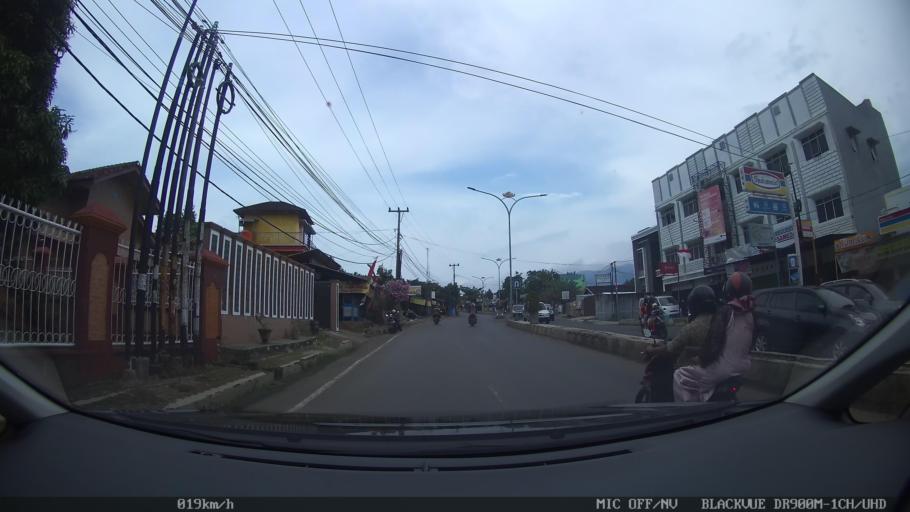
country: ID
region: Lampung
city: Kedaton
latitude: -5.3863
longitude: 105.2212
